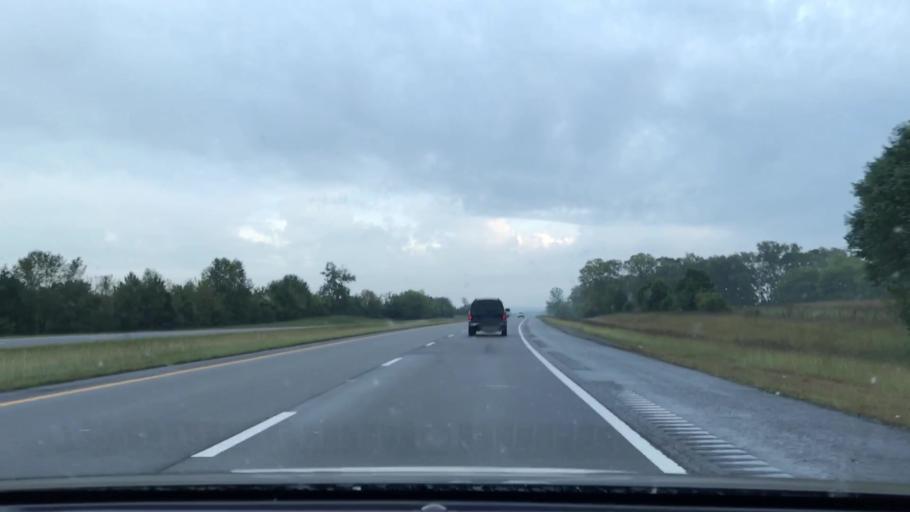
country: US
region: Tennessee
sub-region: Sumner County
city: Gallatin
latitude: 36.4028
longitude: -86.4777
